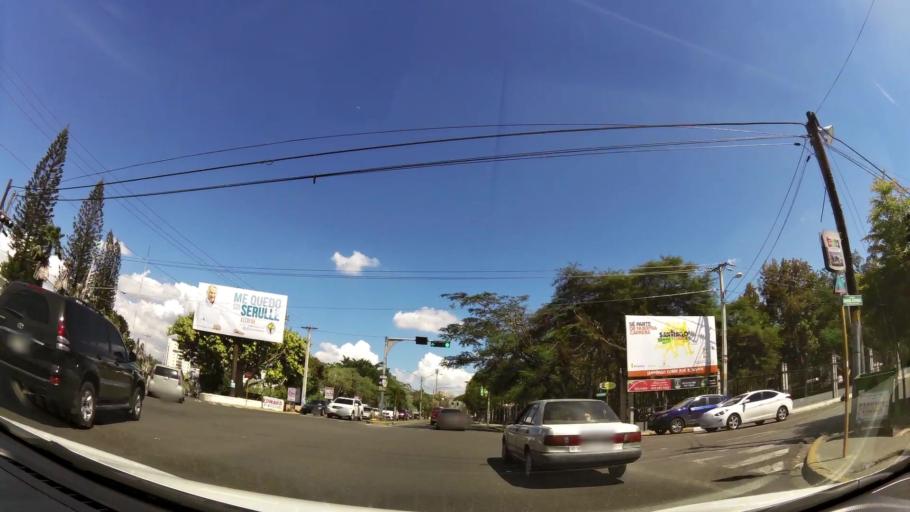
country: DO
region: Santiago
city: Santiago de los Caballeros
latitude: 19.4525
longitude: -70.6935
